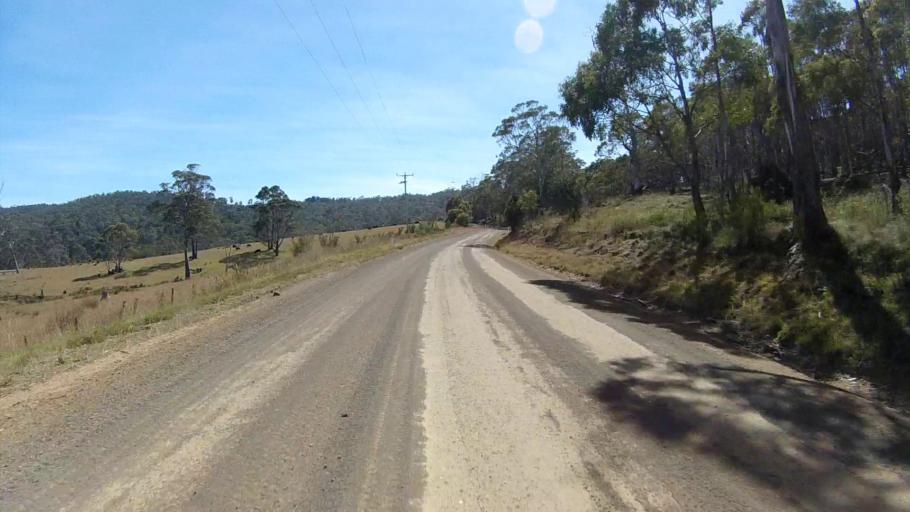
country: AU
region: Tasmania
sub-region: Sorell
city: Sorell
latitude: -42.7446
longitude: 147.7293
